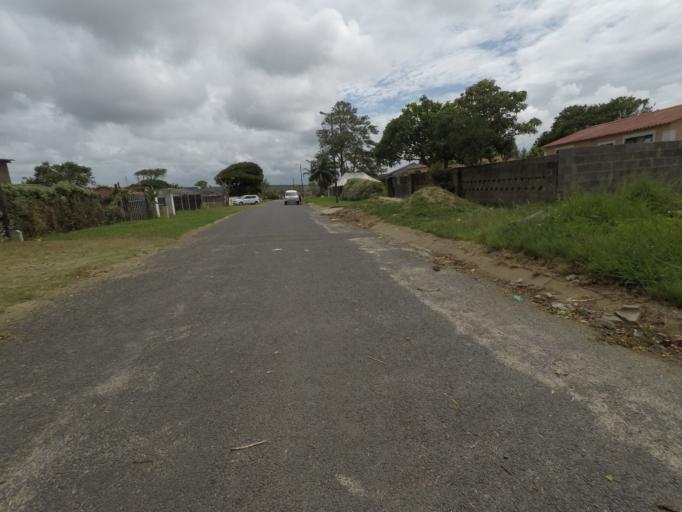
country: ZA
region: KwaZulu-Natal
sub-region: uThungulu District Municipality
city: eSikhawini
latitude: -28.8814
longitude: 31.9012
